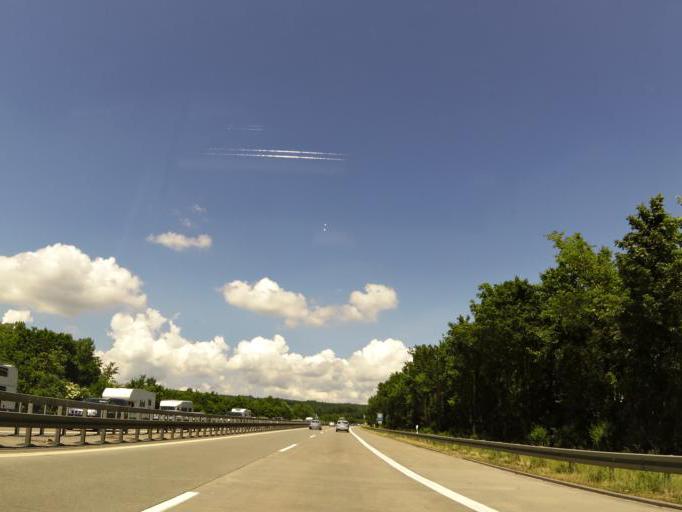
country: DE
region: Baden-Wuerttemberg
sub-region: Tuebingen Region
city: Langenau
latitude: 48.4936
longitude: 10.0882
